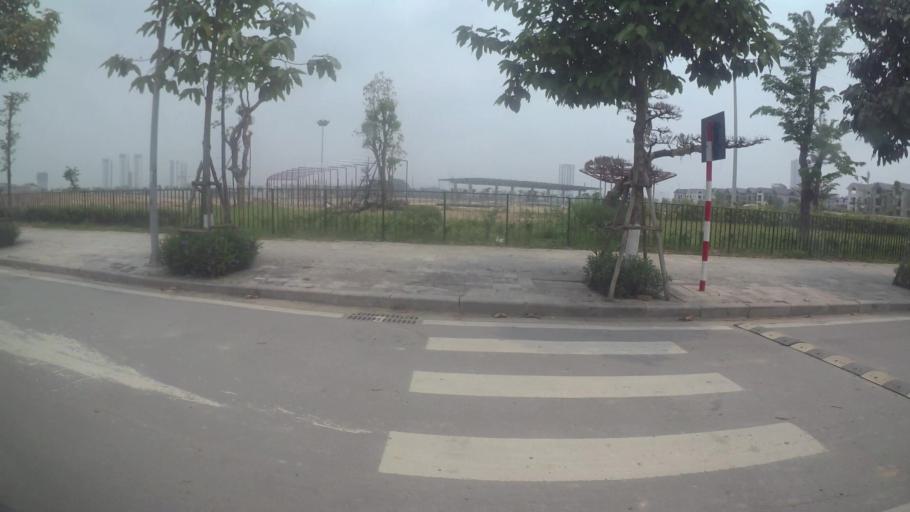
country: VN
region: Ha Noi
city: Ha Dong
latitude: 20.9790
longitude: 105.7578
